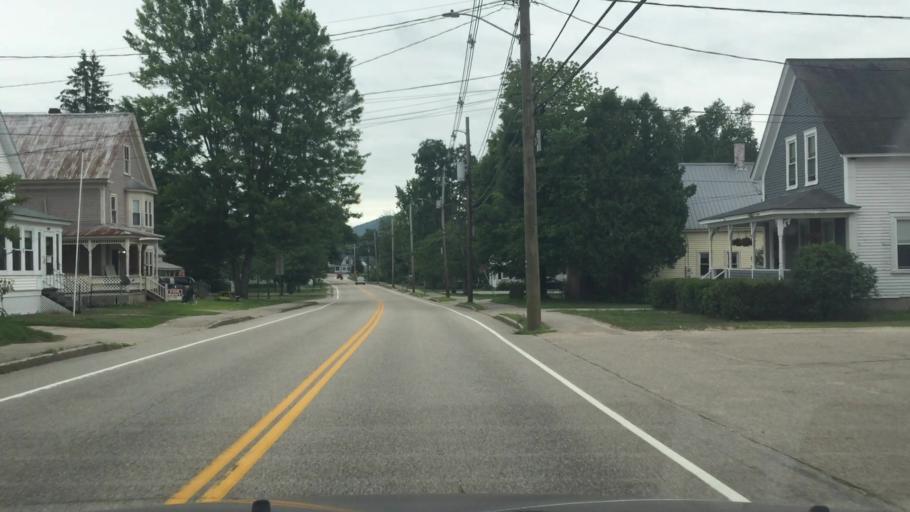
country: US
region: New Hampshire
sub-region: Carroll County
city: Conway
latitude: 43.9771
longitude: -71.1181
